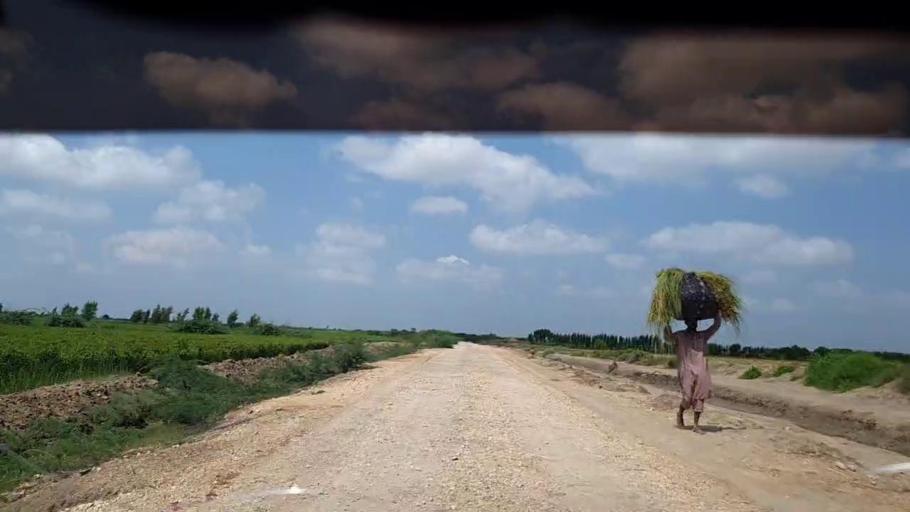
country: PK
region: Sindh
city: Kadhan
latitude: 24.5897
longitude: 68.9682
